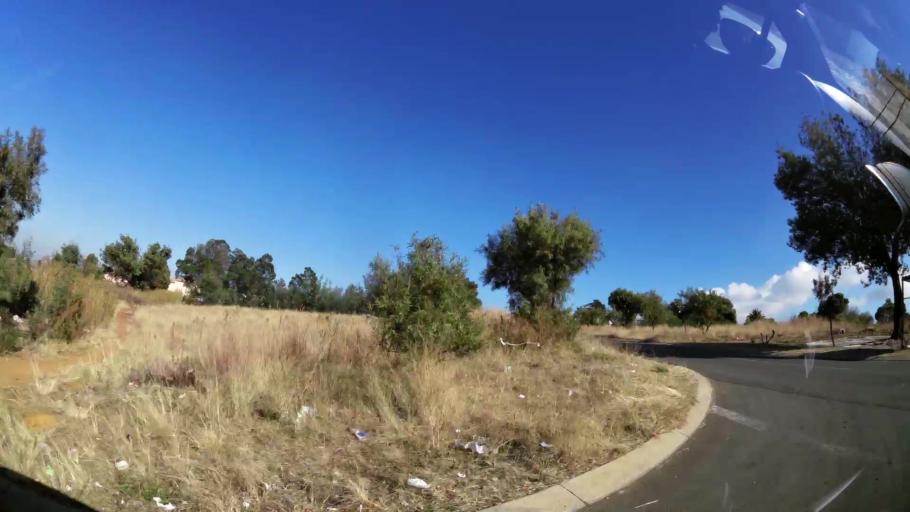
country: ZA
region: Gauteng
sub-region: City of Johannesburg Metropolitan Municipality
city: Roodepoort
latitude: -26.1561
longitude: 27.8337
